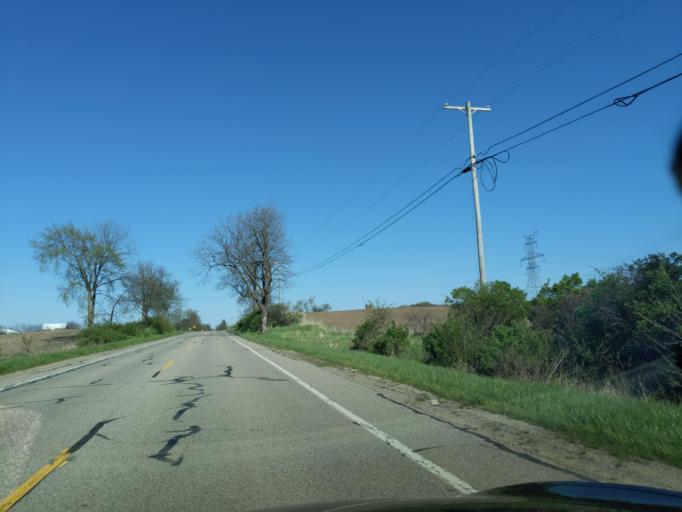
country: US
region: Michigan
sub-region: Kent County
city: Forest Hills
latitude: 42.8853
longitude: -85.4271
